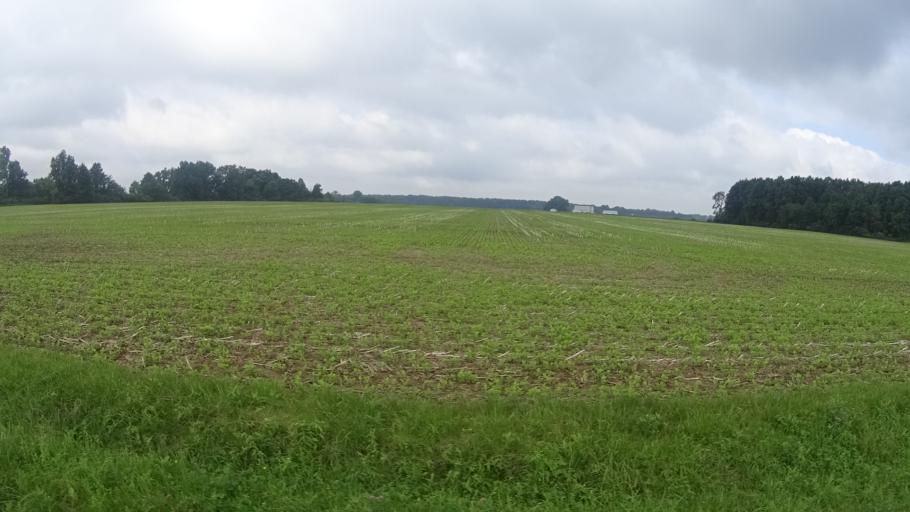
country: US
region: Ohio
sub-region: Huron County
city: Wakeman
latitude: 41.2921
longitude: -82.4809
